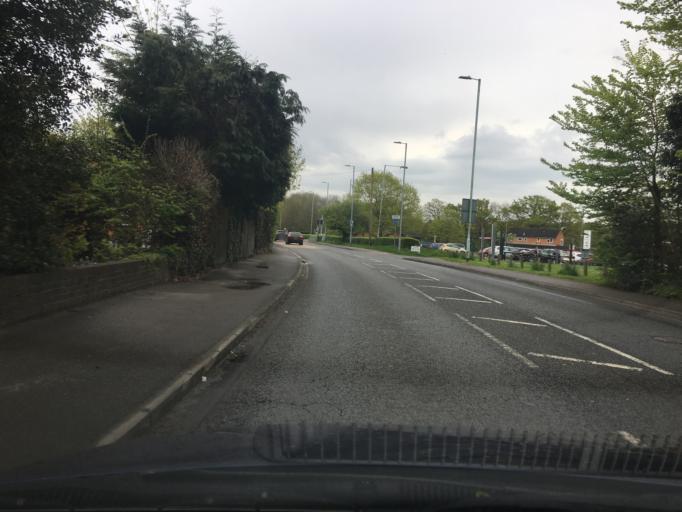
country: GB
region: England
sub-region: Bracknell Forest
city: Sandhurst
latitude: 51.3449
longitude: -0.7937
